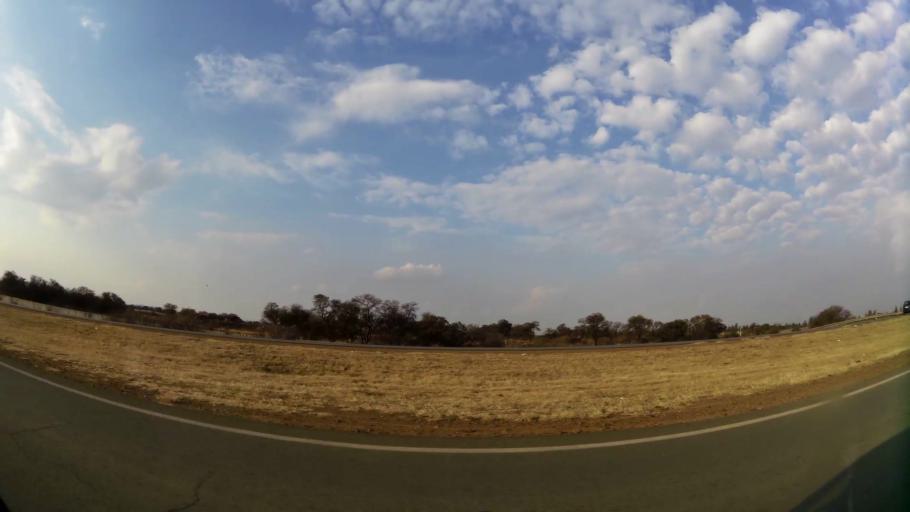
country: ZA
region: Gauteng
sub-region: Sedibeng District Municipality
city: Vereeniging
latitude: -26.6364
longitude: 27.8706
